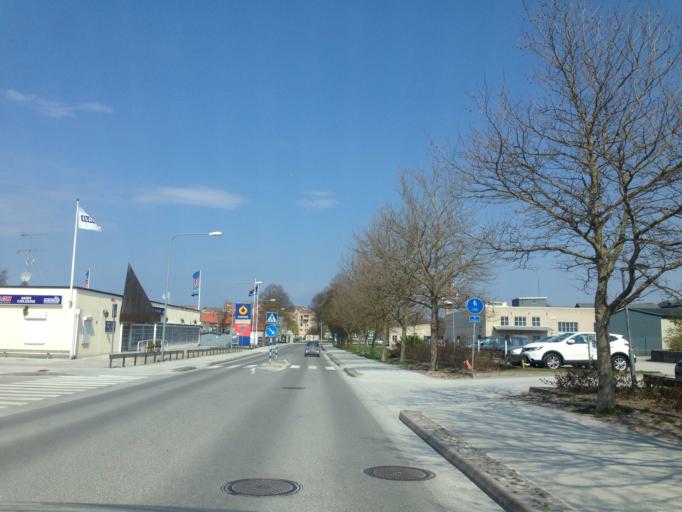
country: SE
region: Gotland
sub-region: Gotland
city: Visby
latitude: 57.6290
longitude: 18.2877
